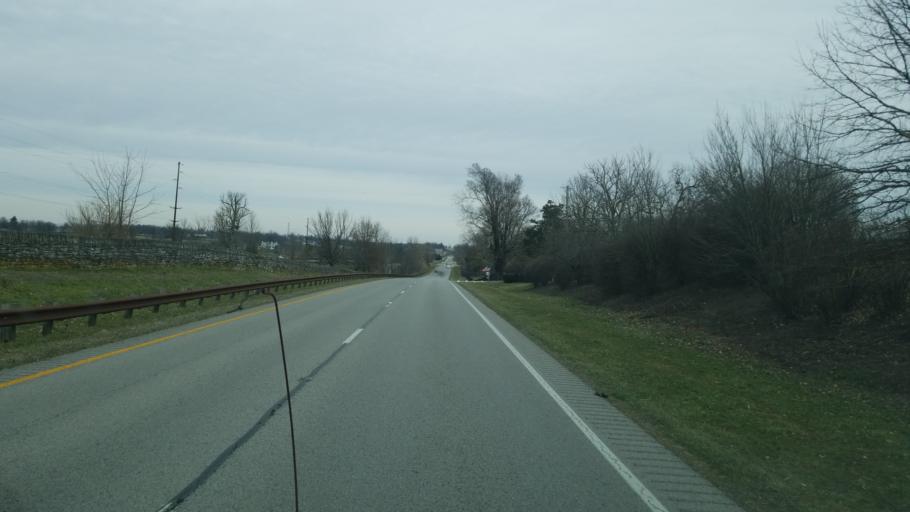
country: US
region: Kentucky
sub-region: Fayette County
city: Lexington-Fayette
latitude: 38.1156
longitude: -84.3953
